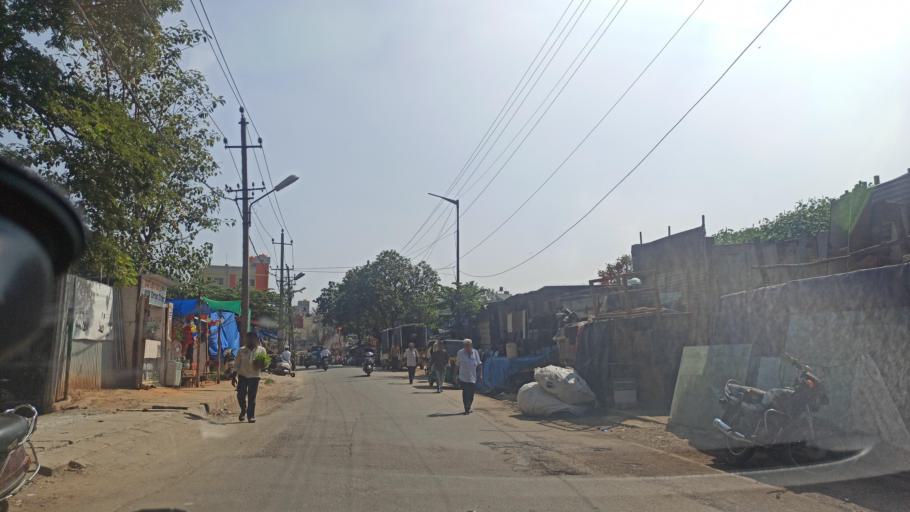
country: IN
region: Karnataka
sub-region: Bangalore Urban
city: Yelahanka
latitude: 13.0394
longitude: 77.5953
